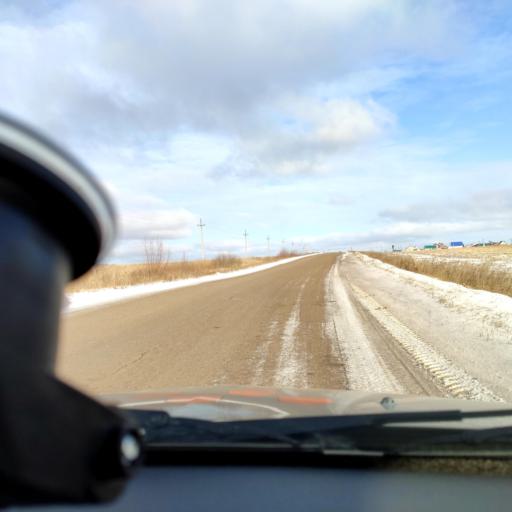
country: RU
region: Bashkortostan
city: Mikhaylovka
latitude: 54.8049
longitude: 55.7795
